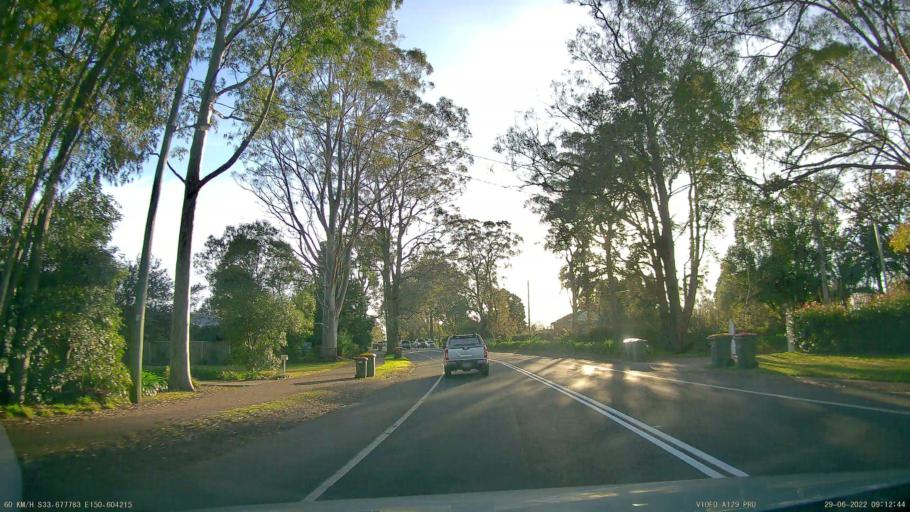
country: AU
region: New South Wales
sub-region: Penrith Municipality
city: Emu Heights
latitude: -33.6775
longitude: 150.6045
